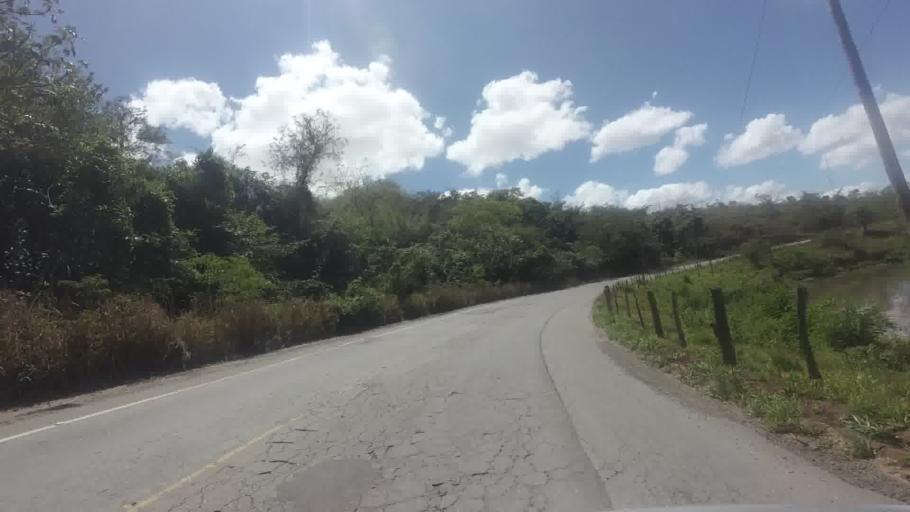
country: BR
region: Rio de Janeiro
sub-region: Santo Antonio De Padua
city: Santo Antonio de Padua
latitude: -21.6574
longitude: -42.3085
